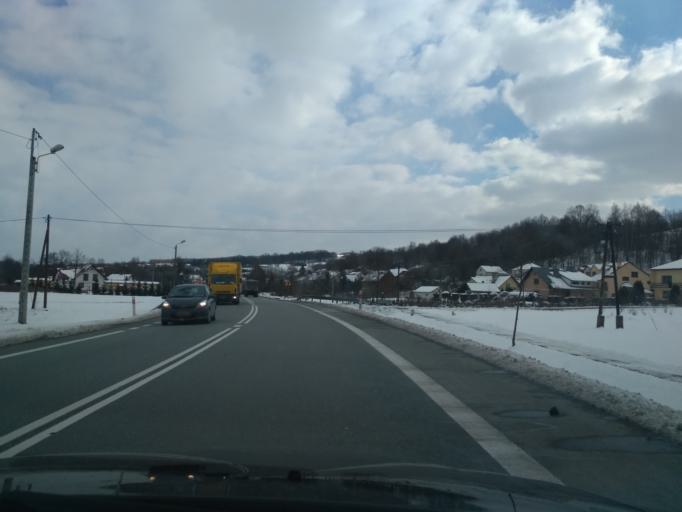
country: PL
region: Subcarpathian Voivodeship
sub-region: Powiat strzyzowski
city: Polomia
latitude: 49.9036
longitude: 21.8680
